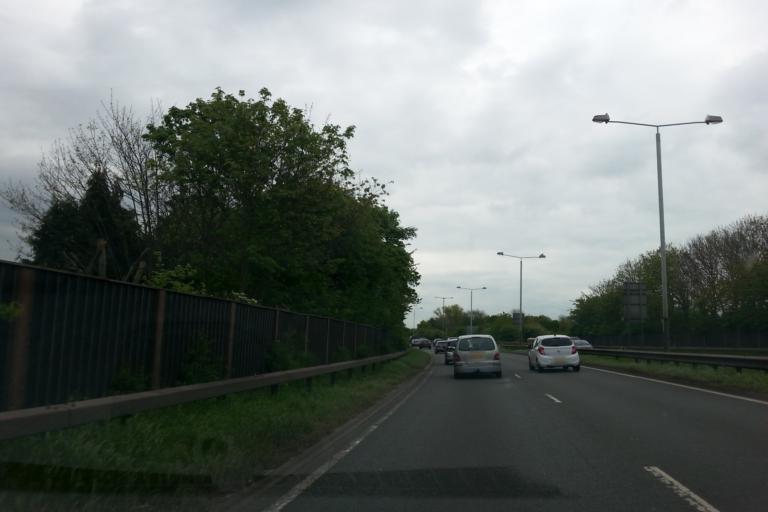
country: GB
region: England
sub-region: Nottinghamshire
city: Ruddington
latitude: 52.9138
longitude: -1.1595
